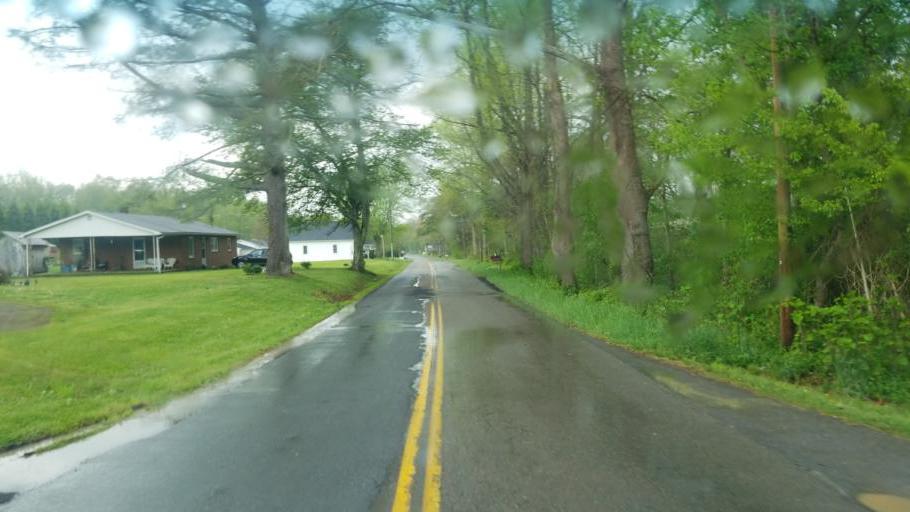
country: US
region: Virginia
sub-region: Smyth County
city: Adwolf
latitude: 36.7678
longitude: -81.5630
